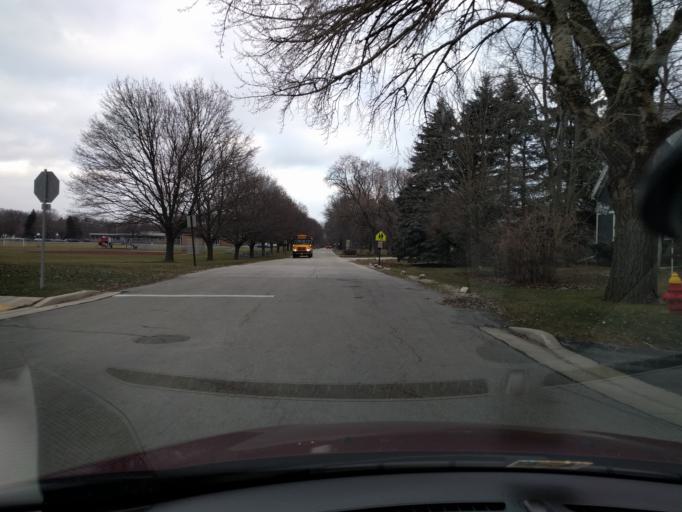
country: US
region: Wisconsin
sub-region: Milwaukee County
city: Glendale
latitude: 43.1227
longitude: -87.9264
